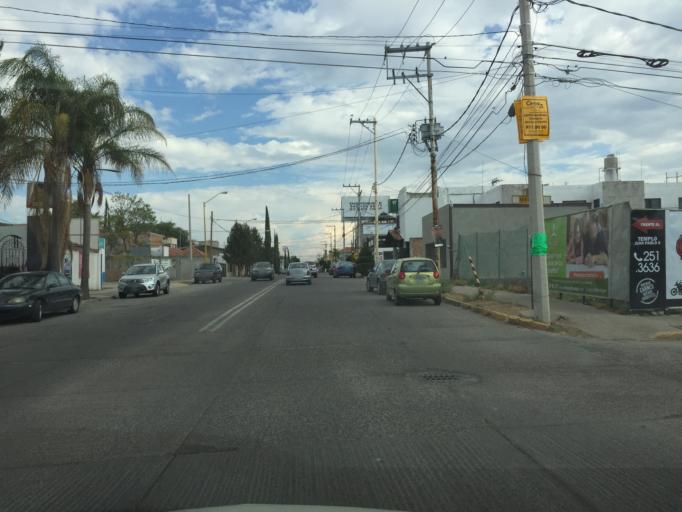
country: MX
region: Aguascalientes
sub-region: Jesus Maria
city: El Llano
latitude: 21.9301
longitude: -102.3053
